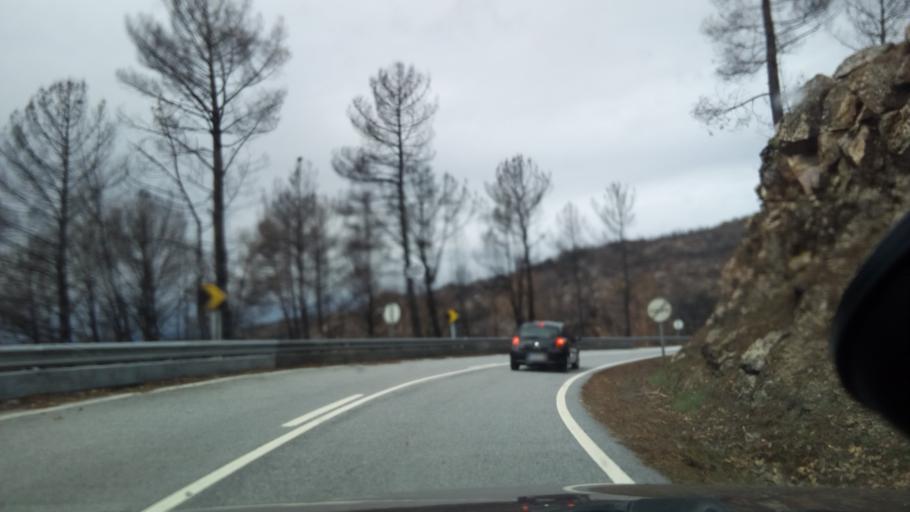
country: PT
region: Guarda
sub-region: Manteigas
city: Manteigas
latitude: 40.4671
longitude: -7.5909
